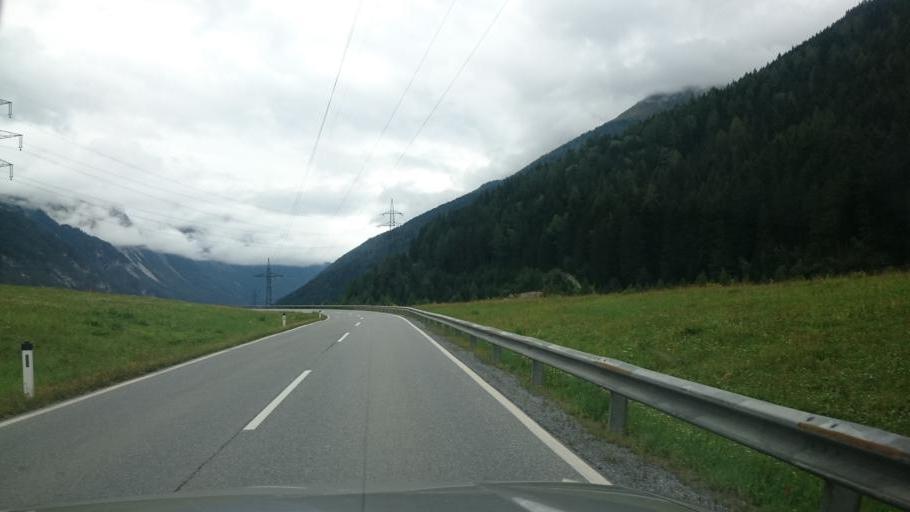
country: AT
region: Tyrol
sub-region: Politischer Bezirk Landeck
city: Sankt Anton am Arlberg
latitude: 47.1435
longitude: 10.3228
